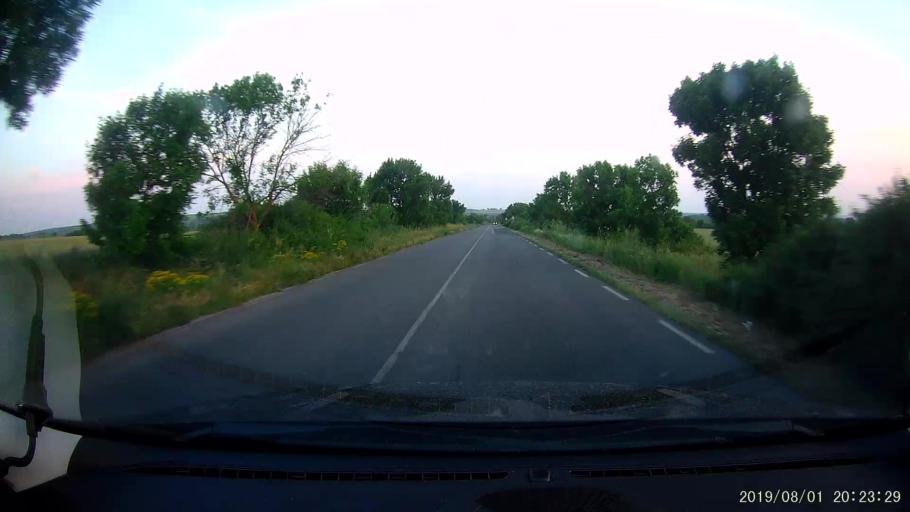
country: BG
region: Yambol
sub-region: Obshtina Elkhovo
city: Elkhovo
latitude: 42.2476
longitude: 26.5989
